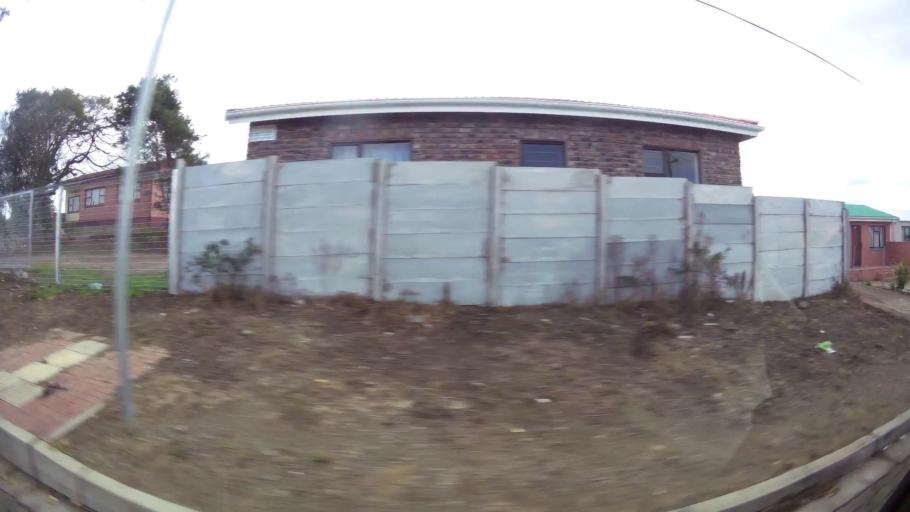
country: ZA
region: Western Cape
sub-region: Eden District Municipality
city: George
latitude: -34.0118
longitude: 22.4570
